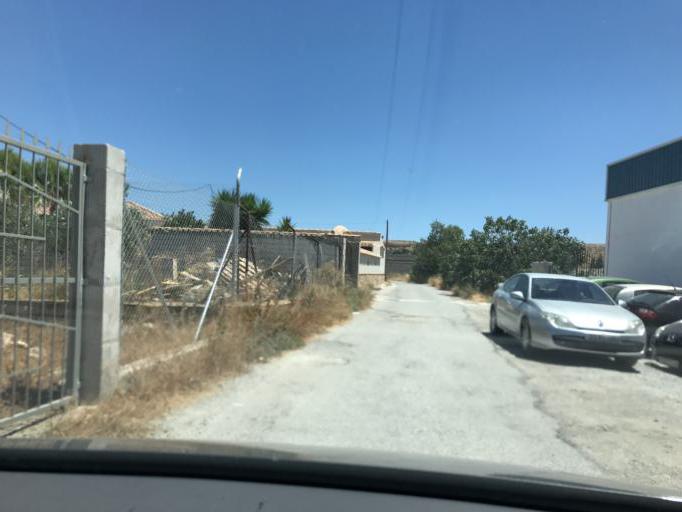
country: ES
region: Andalusia
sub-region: Provincia de Almeria
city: Albox
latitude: 37.3993
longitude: -2.1523
